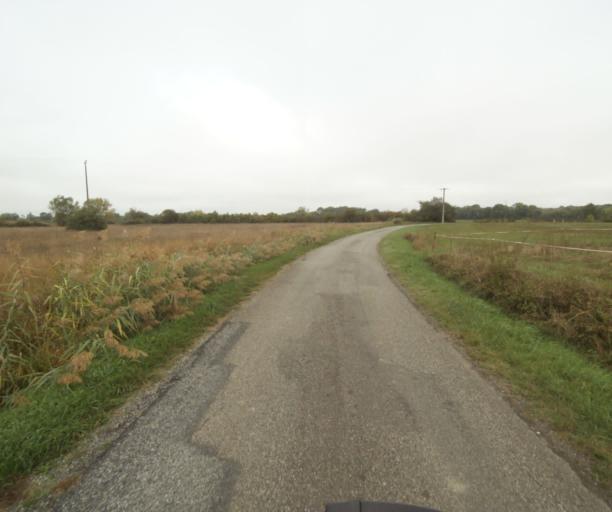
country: FR
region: Midi-Pyrenees
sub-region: Departement du Tarn-et-Garonne
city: Orgueil
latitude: 43.8997
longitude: 1.3857
